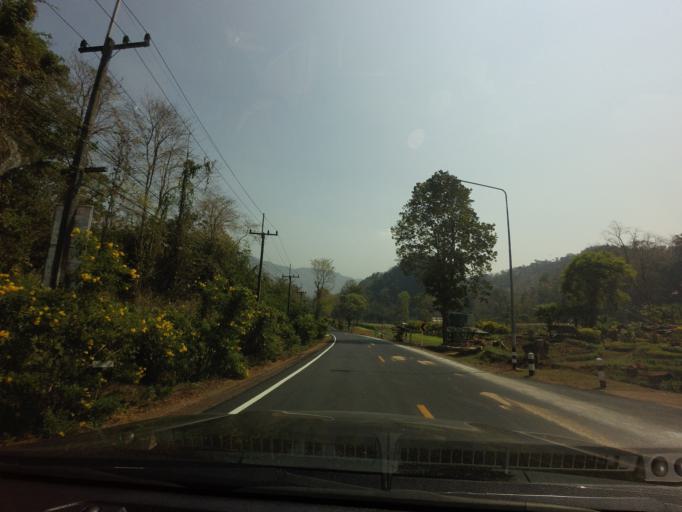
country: TH
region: Kanchanaburi
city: Thong Pha Phum
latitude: 14.7783
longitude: 98.5892
